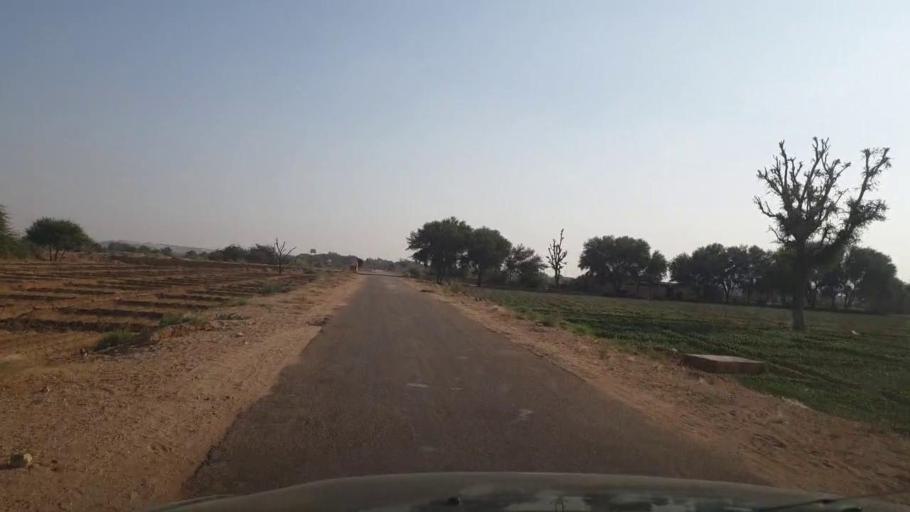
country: PK
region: Sindh
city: Jamshoro
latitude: 25.3340
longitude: 67.8429
